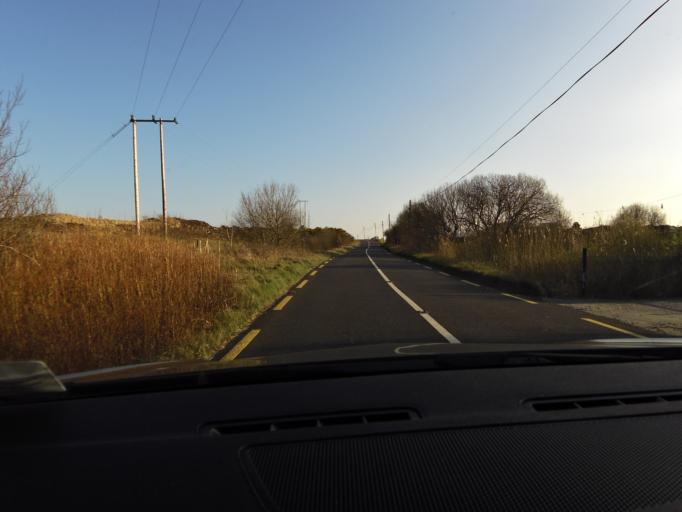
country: IE
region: Connaught
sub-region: County Galway
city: Oughterard
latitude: 53.3667
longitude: -9.5431
